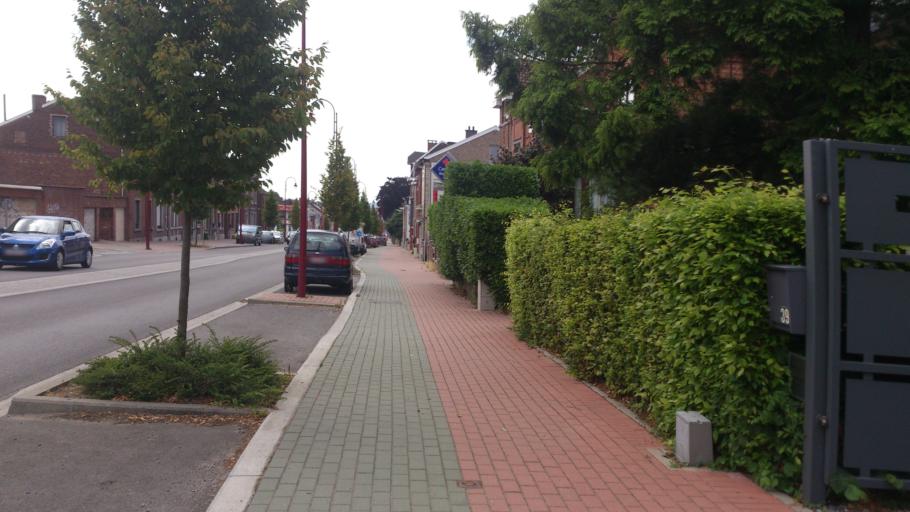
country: BE
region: Wallonia
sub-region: Province de Liege
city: Beyne-Heusay
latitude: 50.6257
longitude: 5.6434
